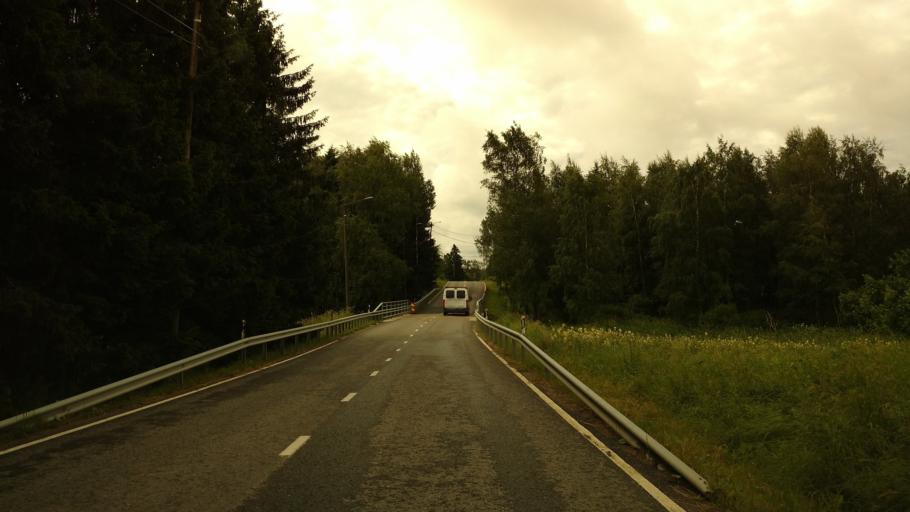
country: FI
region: Varsinais-Suomi
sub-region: Salo
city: Kuusjoki
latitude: 60.5374
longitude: 23.1678
